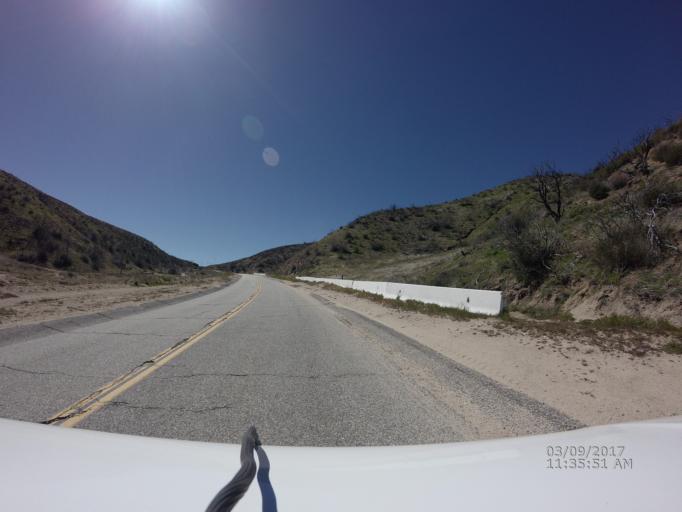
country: US
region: California
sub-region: Los Angeles County
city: Green Valley
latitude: 34.6765
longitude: -118.3941
